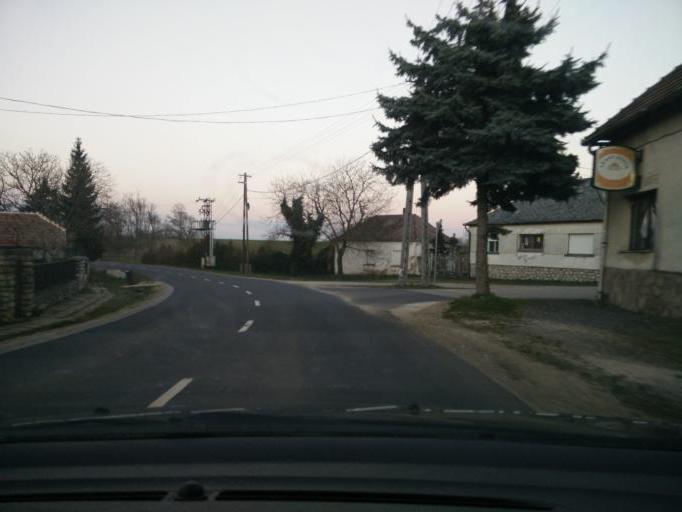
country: HU
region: Veszprem
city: Csabrendek
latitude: 47.0444
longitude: 17.3279
